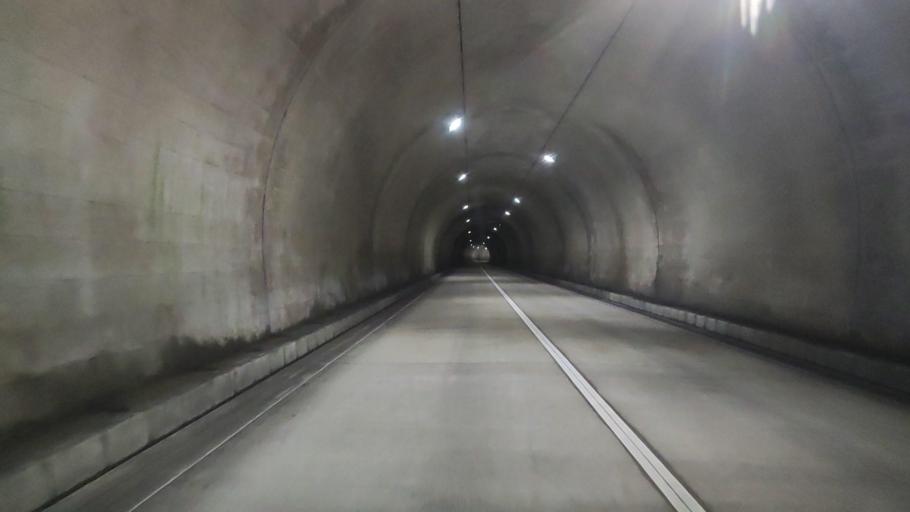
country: JP
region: Wakayama
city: Shingu
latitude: 33.8709
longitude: 135.8568
